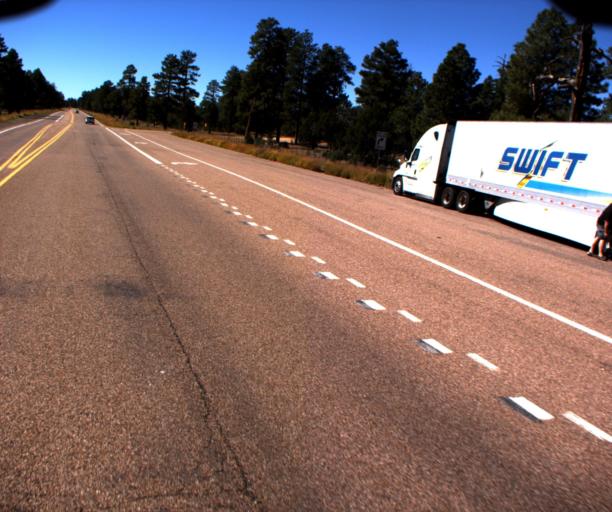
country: US
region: Arizona
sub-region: Navajo County
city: Heber-Overgaard
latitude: 34.4313
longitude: -110.6421
